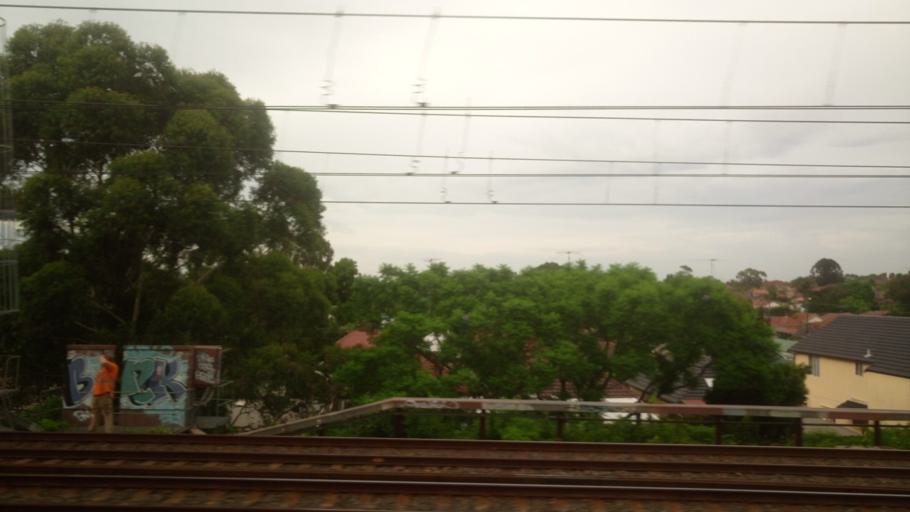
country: AU
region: New South Wales
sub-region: Ashfield
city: Croydon
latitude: -33.8849
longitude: 151.1188
